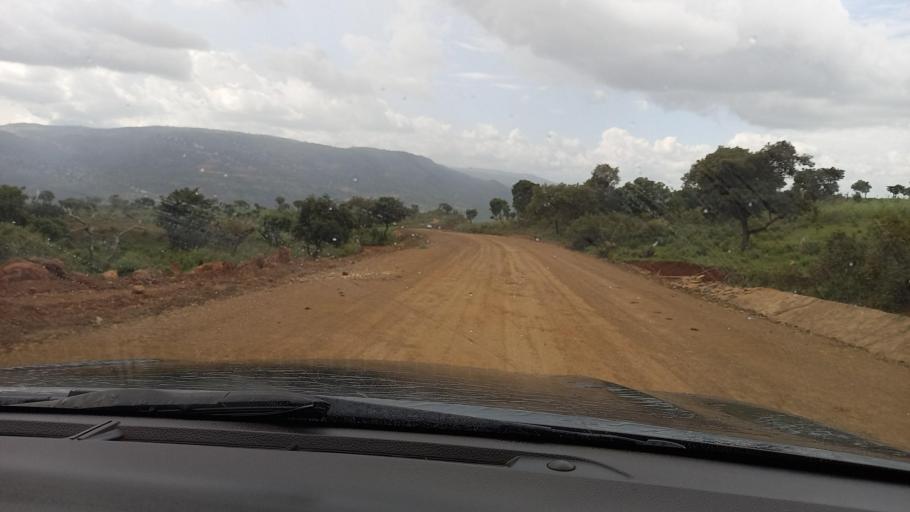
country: ET
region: Southern Nations, Nationalities, and People's Region
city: Mizan Teferi
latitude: 6.1780
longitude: 35.7027
